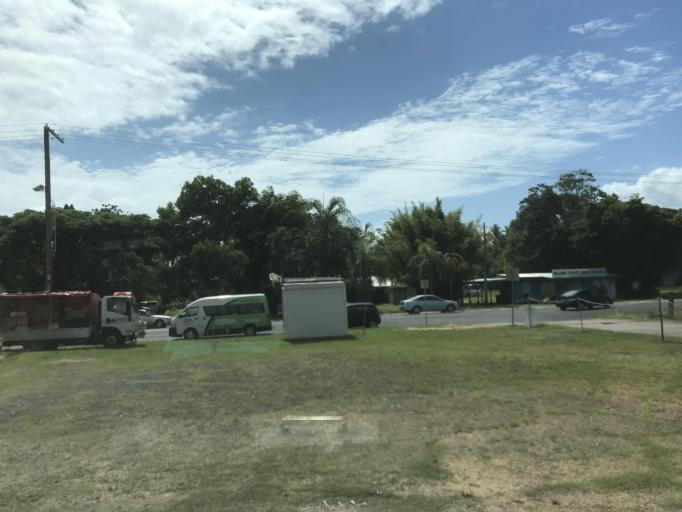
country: AU
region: Queensland
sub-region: Cassowary Coast
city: Innisfail
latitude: -17.8678
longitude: 146.1067
